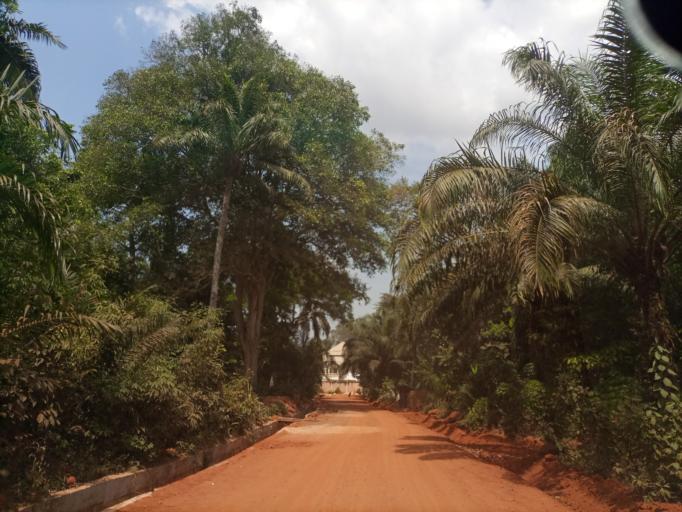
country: NG
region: Enugu
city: Obollo-Afor
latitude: 6.8657
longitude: 7.4732
